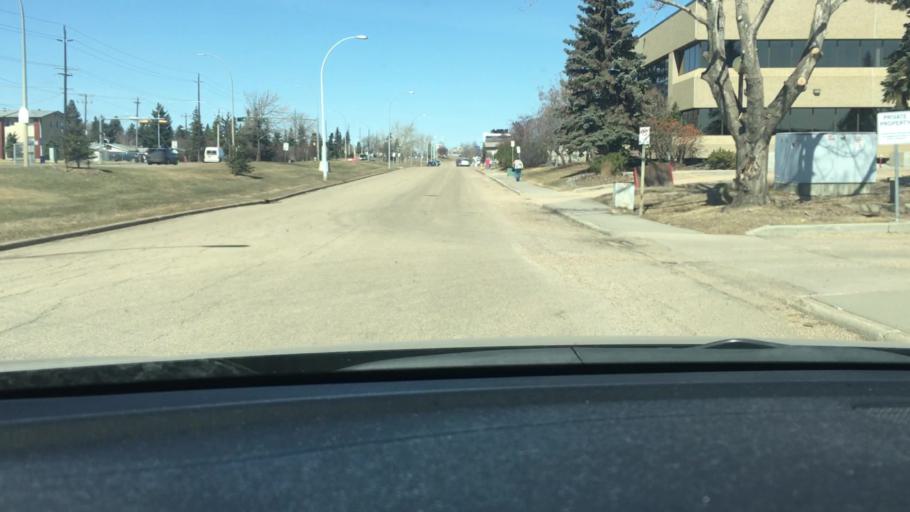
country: CA
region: Alberta
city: Edmonton
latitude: 53.5327
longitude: -113.4181
